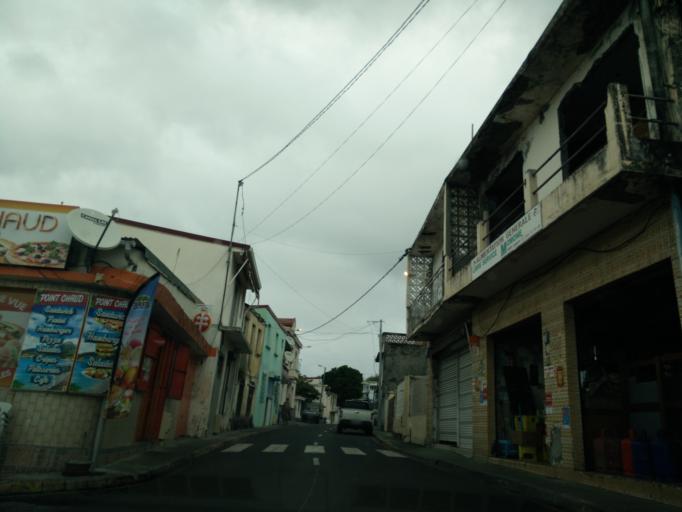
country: MQ
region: Martinique
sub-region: Martinique
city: Saint-Pierre
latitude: 14.8006
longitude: -61.2244
